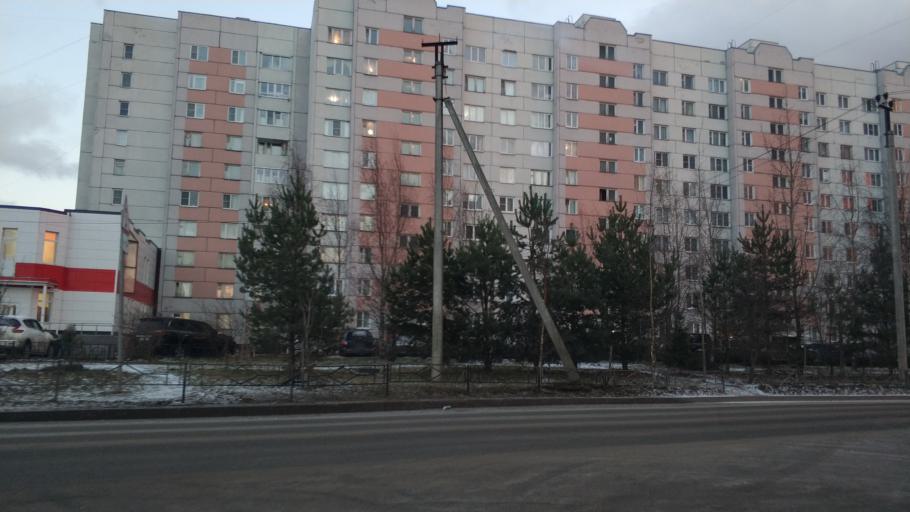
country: RU
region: St.-Petersburg
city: Pontonnyy
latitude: 59.8002
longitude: 30.6376
